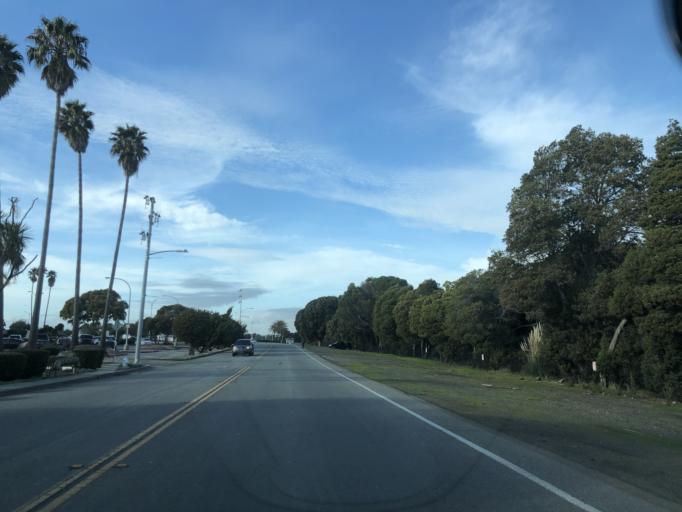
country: US
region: California
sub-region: Alameda County
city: San Leandro
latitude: 37.6976
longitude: -122.1881
